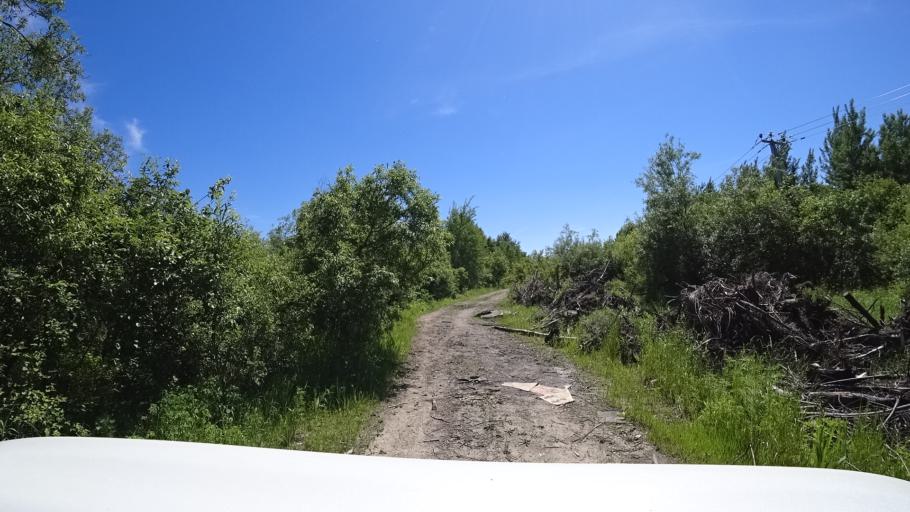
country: RU
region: Khabarovsk Krai
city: Topolevo
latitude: 48.4881
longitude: 135.1773
